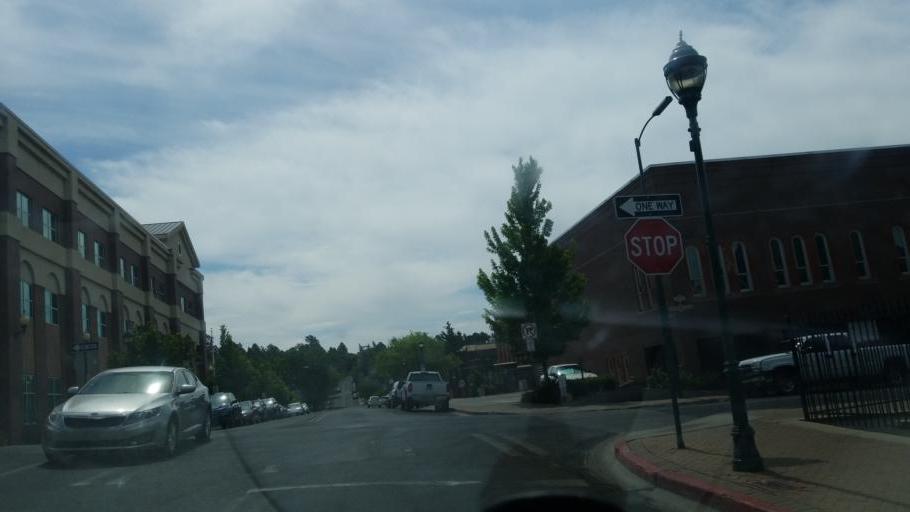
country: US
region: Arizona
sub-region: Coconino County
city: Flagstaff
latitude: 35.2000
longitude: -111.6470
